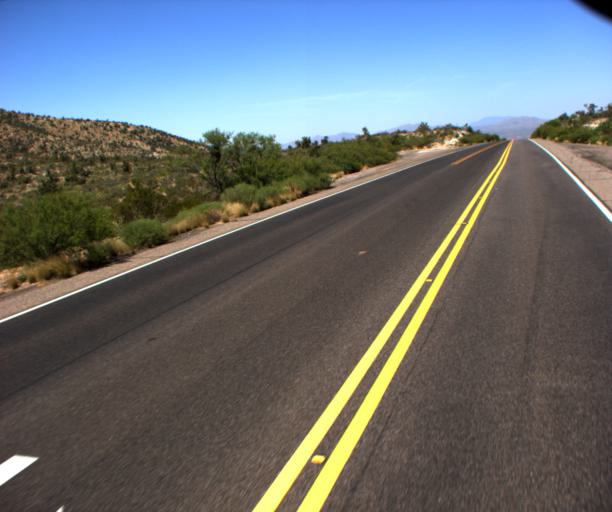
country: US
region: Arizona
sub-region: Gila County
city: Peridot
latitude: 33.2864
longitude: -110.3727
